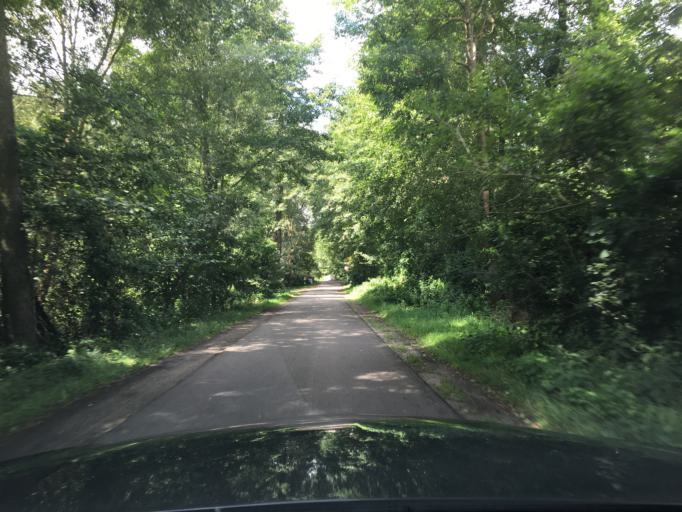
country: DE
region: Brandenburg
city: Vetschau
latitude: 51.8275
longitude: 14.1011
